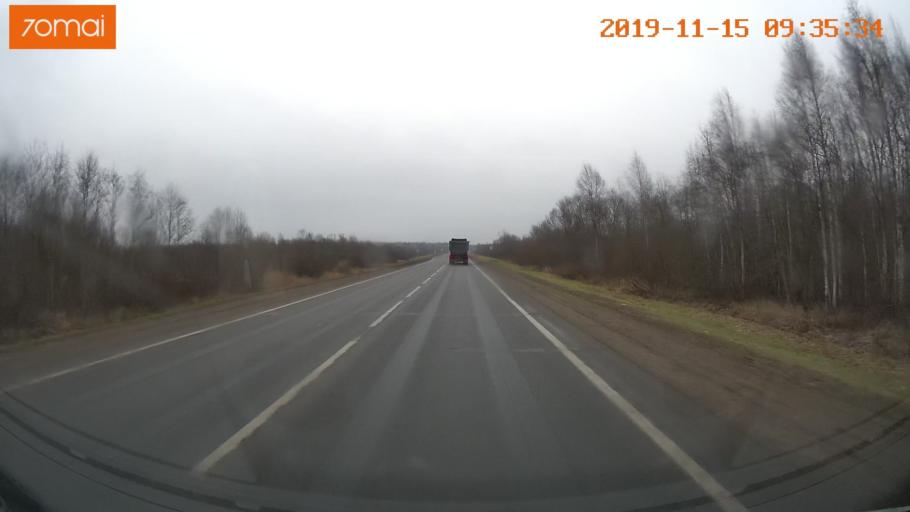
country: RU
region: Vologda
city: Sheksna
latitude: 59.2535
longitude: 38.4022
